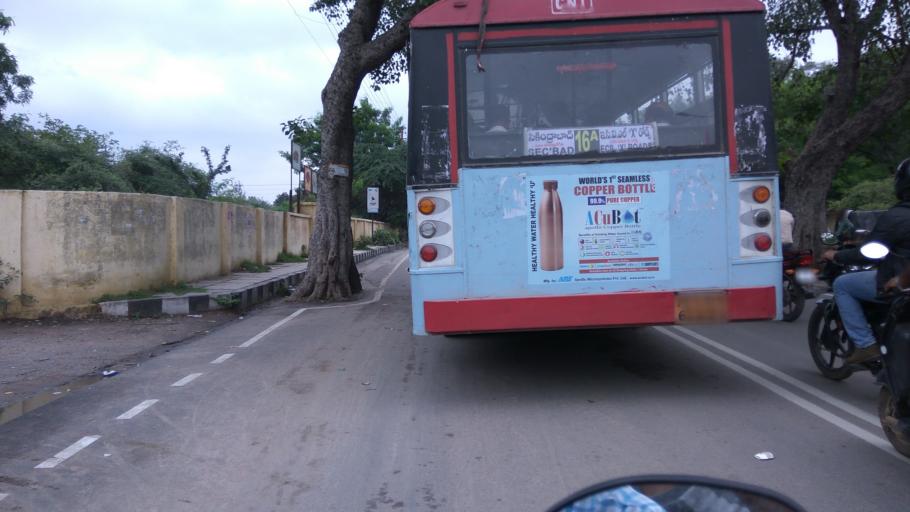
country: IN
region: Telangana
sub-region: Hyderabad
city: Malkajgiri
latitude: 17.4391
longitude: 78.5293
